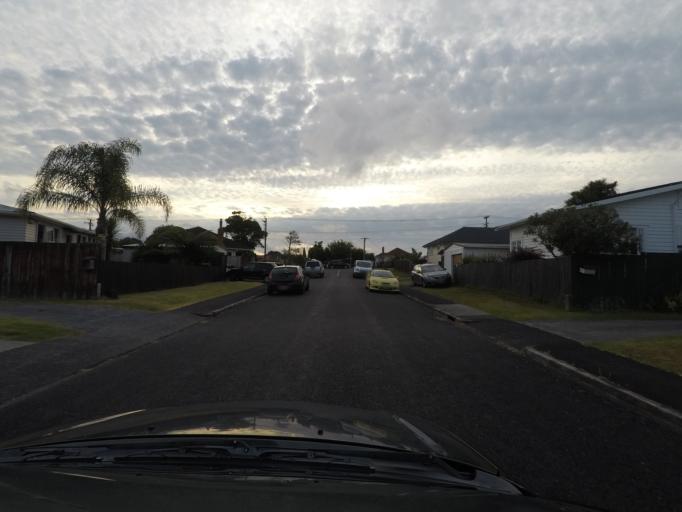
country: NZ
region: Auckland
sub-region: Auckland
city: Rosebank
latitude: -36.8359
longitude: 174.6509
